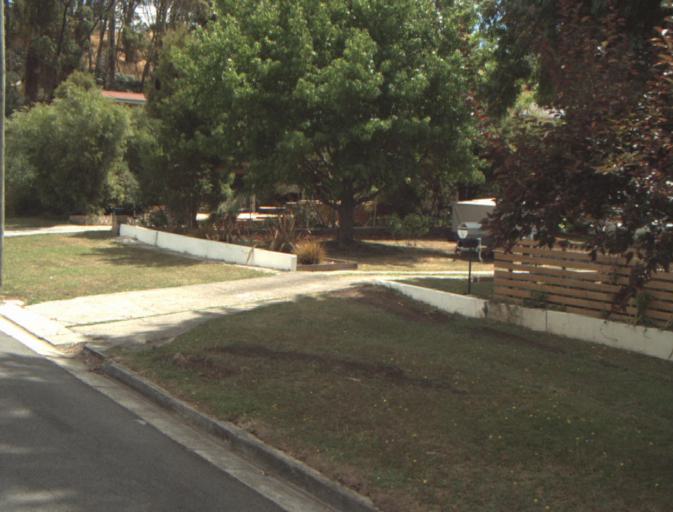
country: AU
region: Tasmania
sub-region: Launceston
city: Launceston
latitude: -41.4363
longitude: 147.1115
